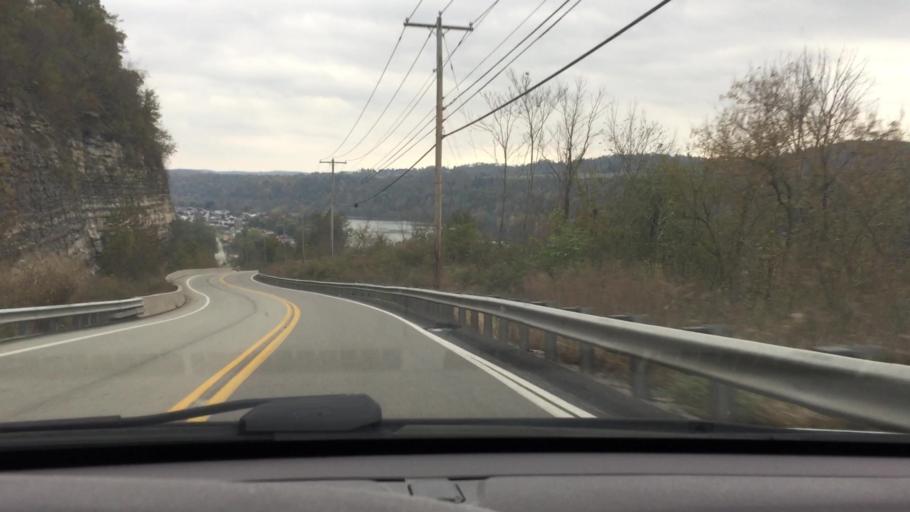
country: US
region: Pennsylvania
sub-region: Washington County
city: California
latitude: 40.0823
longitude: -79.8877
